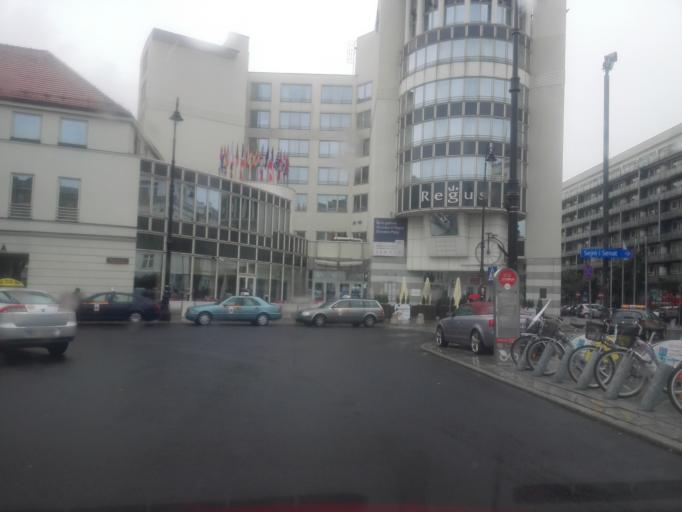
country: PL
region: Masovian Voivodeship
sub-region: Warszawa
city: Srodmiescie
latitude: 52.2278
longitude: 21.0235
